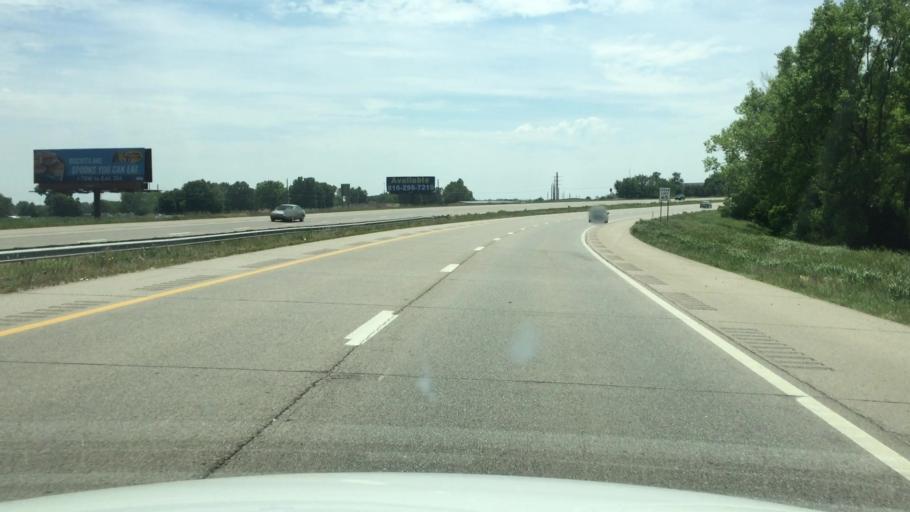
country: US
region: Kansas
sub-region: Shawnee County
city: Topeka
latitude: 39.0988
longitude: -95.7203
